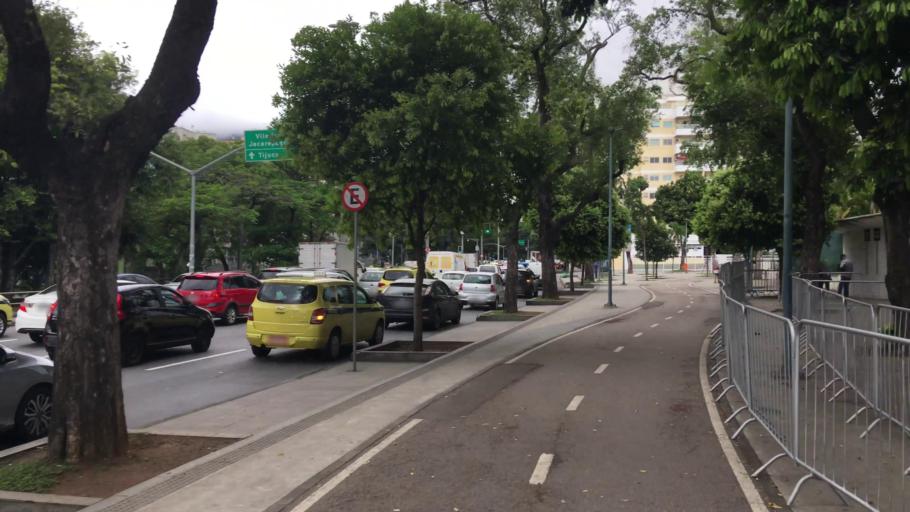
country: BR
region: Rio de Janeiro
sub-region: Rio De Janeiro
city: Rio de Janeiro
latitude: -22.9142
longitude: -43.2284
